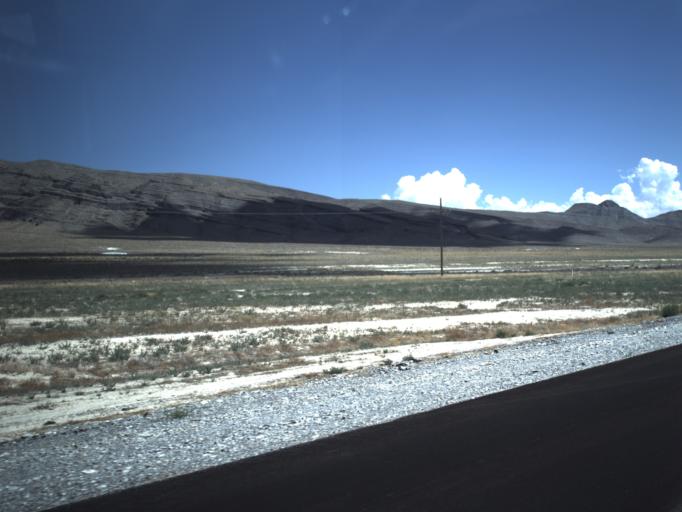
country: US
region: Utah
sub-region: Beaver County
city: Milford
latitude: 39.0588
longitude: -113.4351
